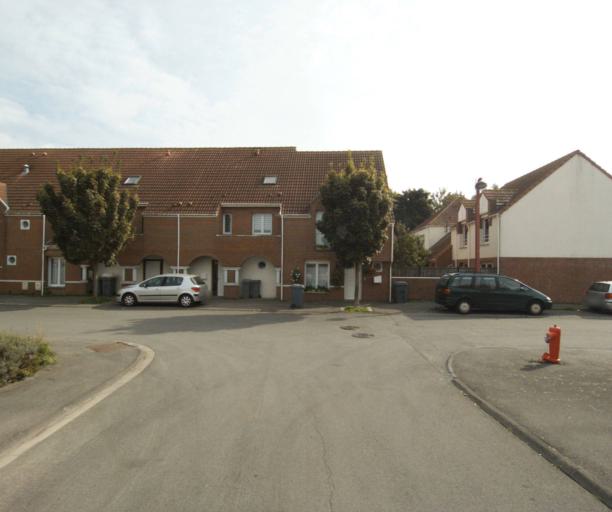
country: FR
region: Nord-Pas-de-Calais
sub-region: Departement du Nord
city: Templemars
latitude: 50.5706
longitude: 3.0533
